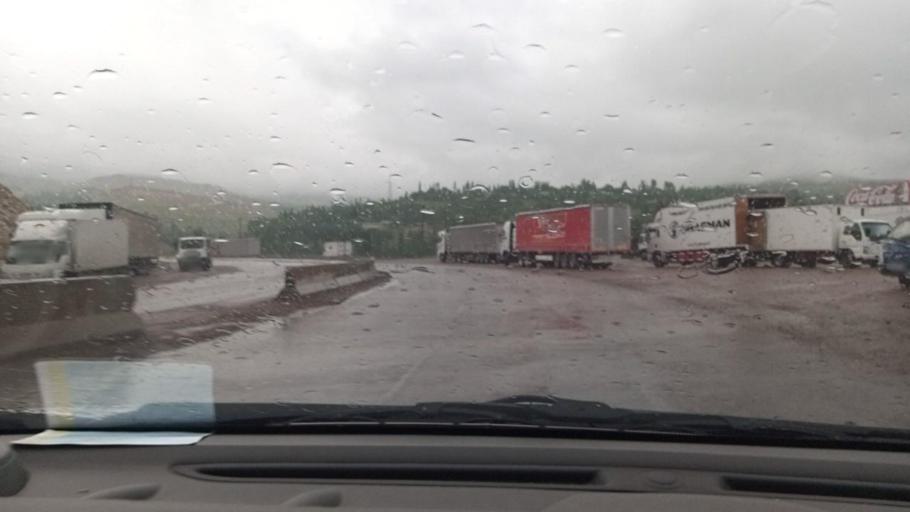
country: UZ
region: Toshkent
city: Angren
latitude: 41.0712
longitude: 70.2515
